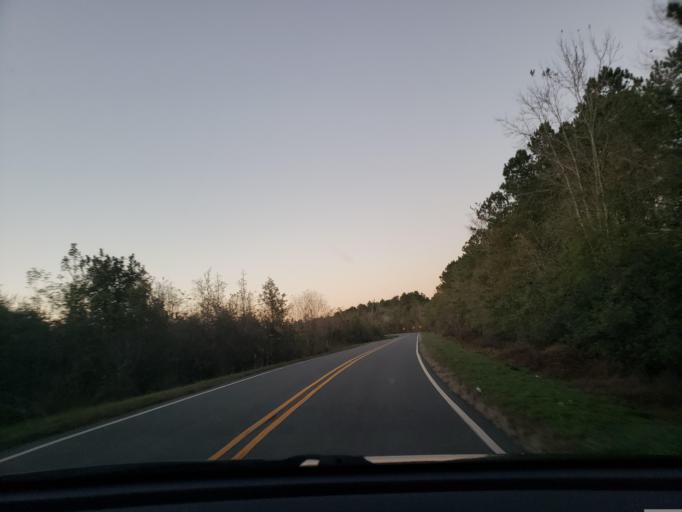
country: US
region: North Carolina
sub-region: Duplin County
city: Beulaville
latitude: 34.7592
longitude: -77.7090
